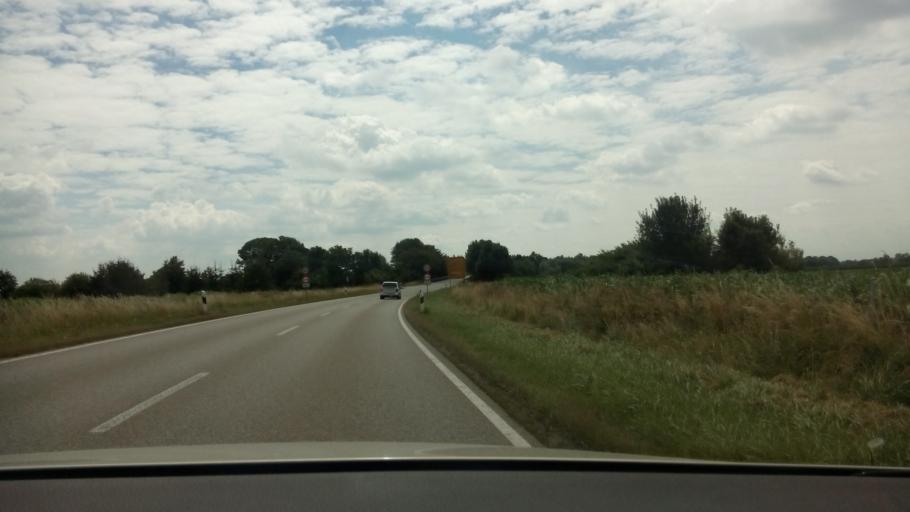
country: DE
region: Bavaria
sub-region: Upper Bavaria
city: Eitting
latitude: 48.3748
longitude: 11.8499
